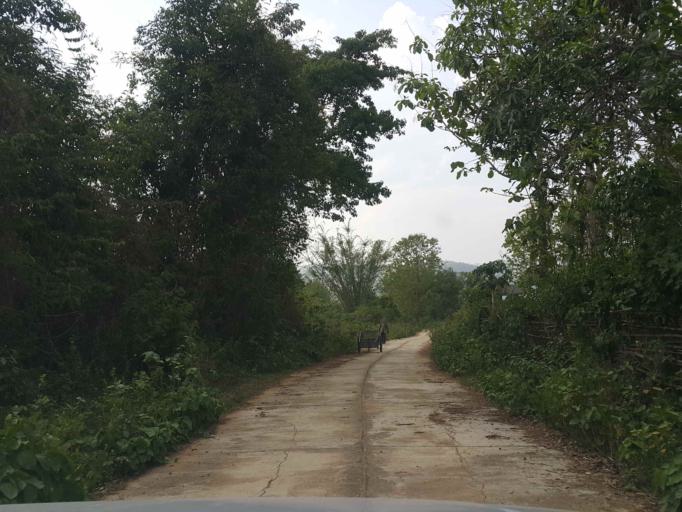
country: TH
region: Chiang Mai
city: Wiang Haeng
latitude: 19.3858
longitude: 98.7232
